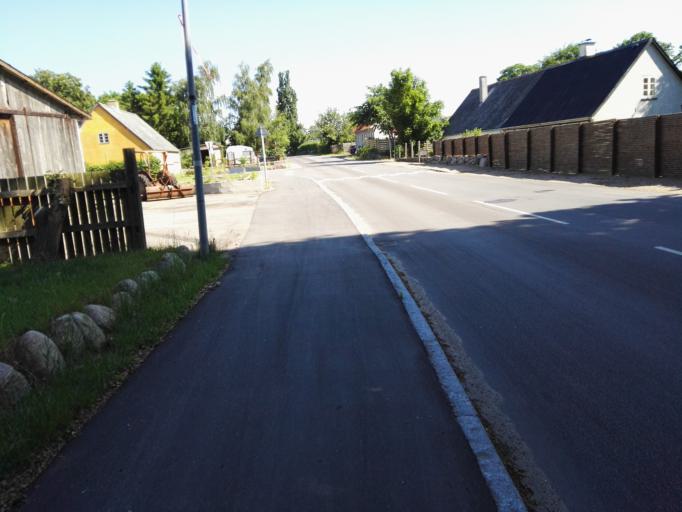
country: DK
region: Zealand
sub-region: Lejre Kommune
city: Ejby
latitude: 55.7181
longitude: 11.8903
